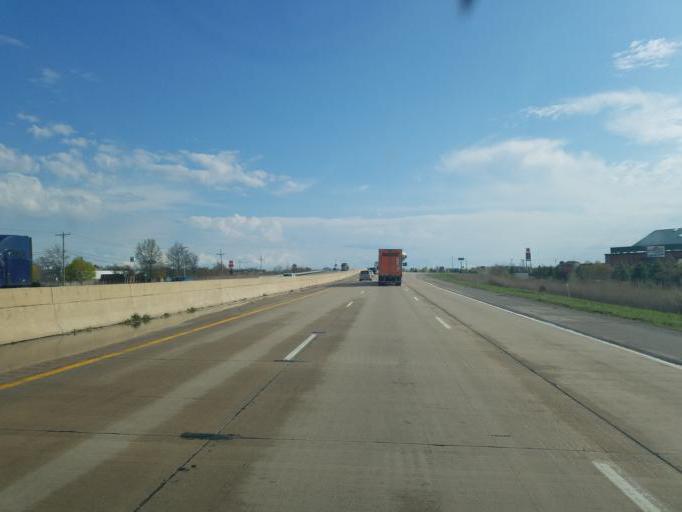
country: US
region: Michigan
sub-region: Monroe County
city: Dundee
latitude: 41.9634
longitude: -83.6726
